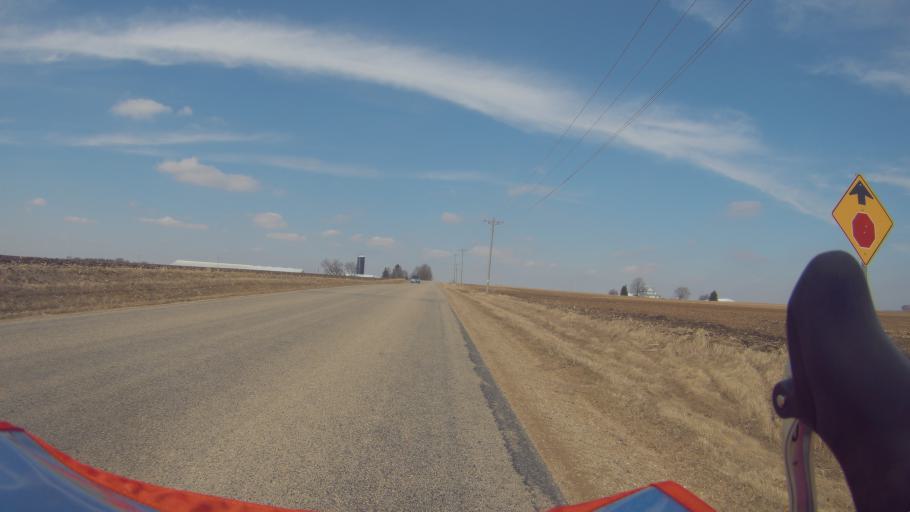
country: US
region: Wisconsin
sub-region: Dane County
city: Waunakee
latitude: 43.1745
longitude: -89.4965
